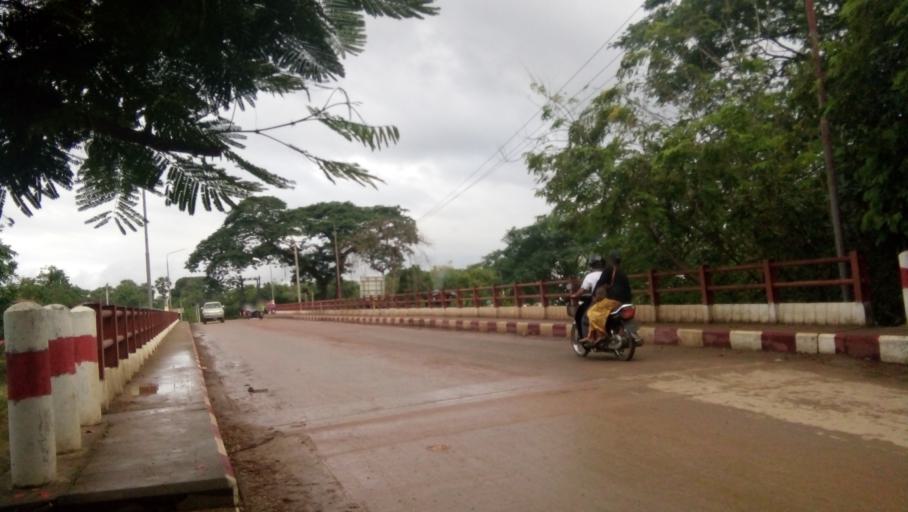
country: MM
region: Kayin
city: Hpa-an
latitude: 17.1207
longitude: 97.8176
